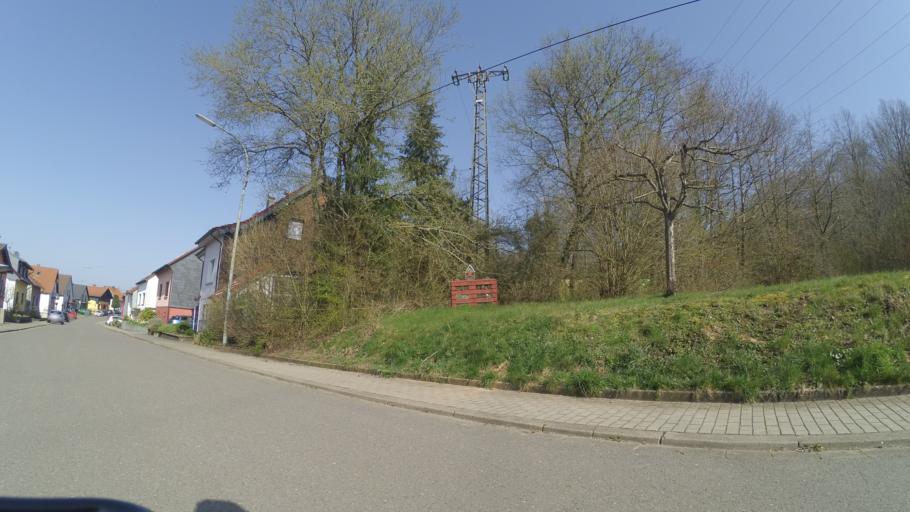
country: DE
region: Saarland
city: Merchweiler
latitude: 49.3390
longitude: 7.0004
